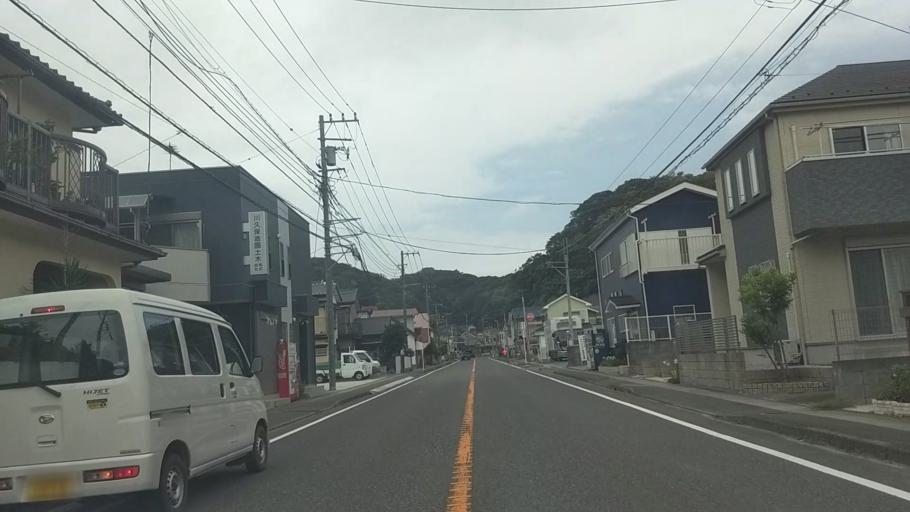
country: JP
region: Kanagawa
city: Yokosuka
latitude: 35.2515
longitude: 139.7368
